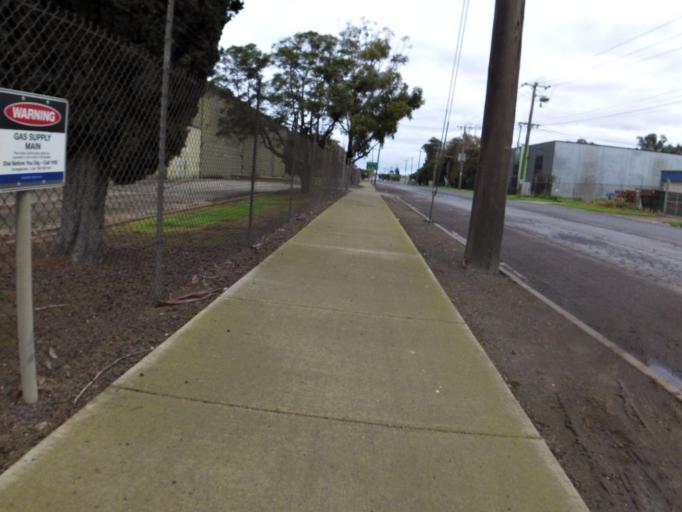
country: AU
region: Victoria
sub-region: Greater Geelong
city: Bell Park
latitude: -38.0943
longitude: 144.3729
